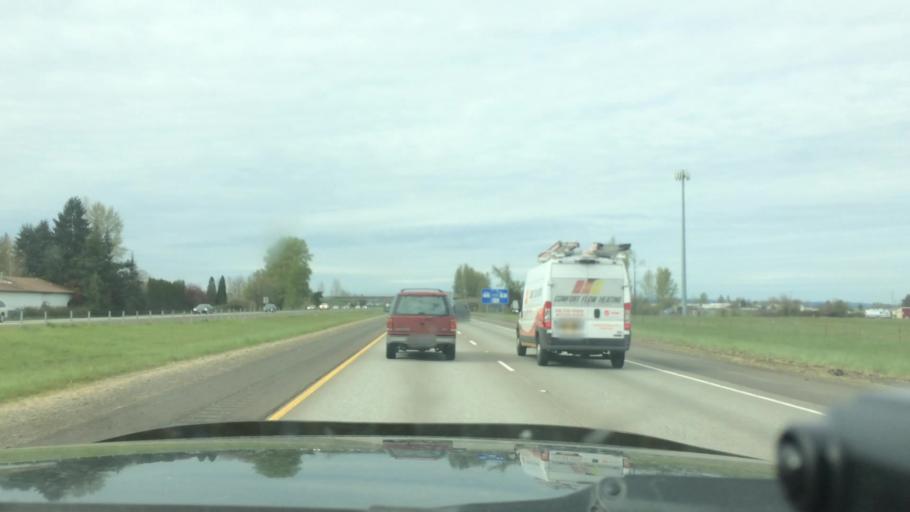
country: US
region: Oregon
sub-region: Linn County
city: Albany
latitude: 44.6066
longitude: -123.0619
